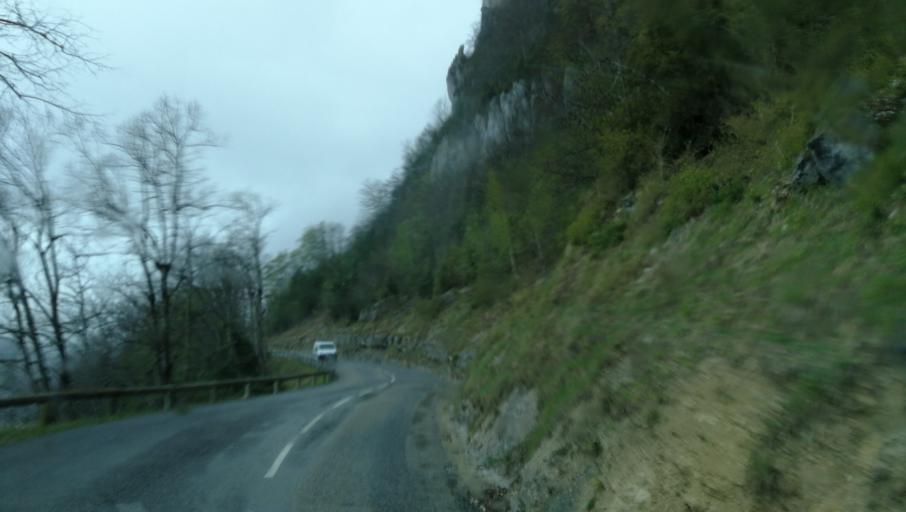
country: FR
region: Rhone-Alpes
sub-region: Departement de la Drome
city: Saint-Laurent-en-Royans
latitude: 44.9926
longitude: 5.3331
